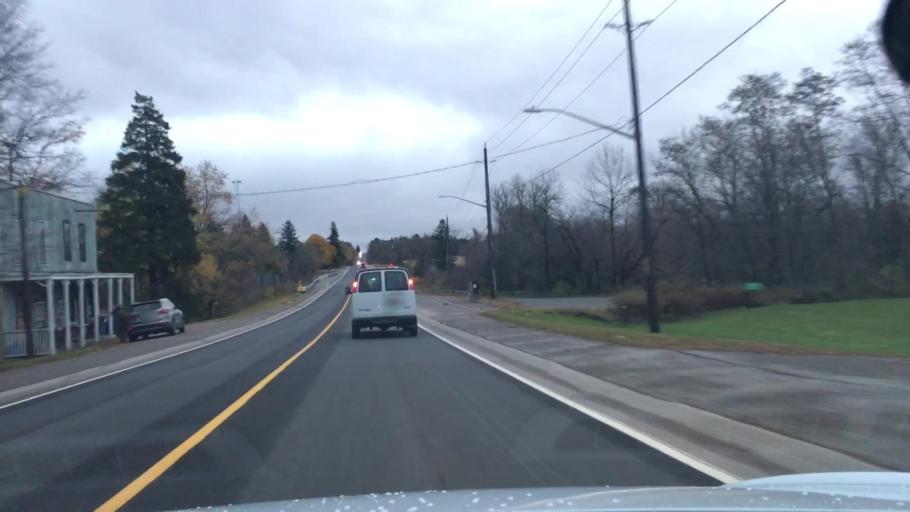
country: CA
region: Ontario
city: Pickering
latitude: 43.9013
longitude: -79.1833
